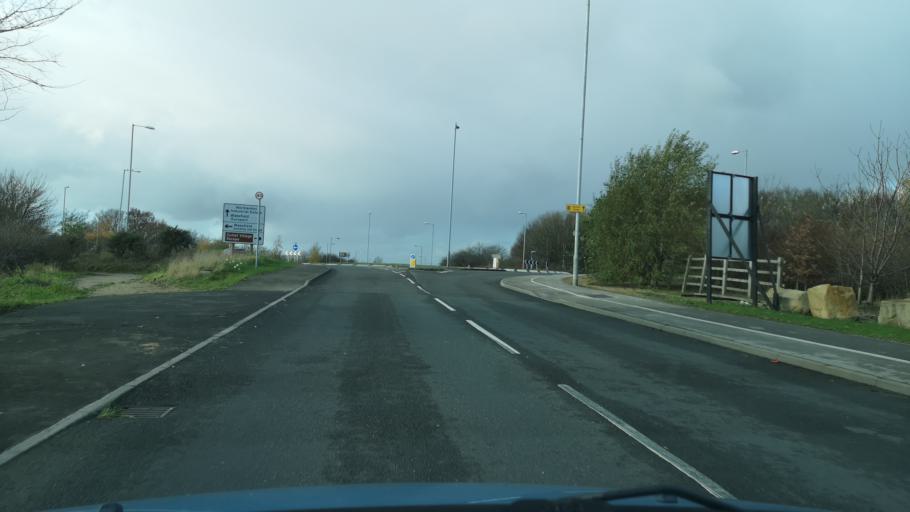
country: GB
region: England
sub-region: City and Borough of Wakefield
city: Normanton
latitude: 53.6989
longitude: -1.3889
